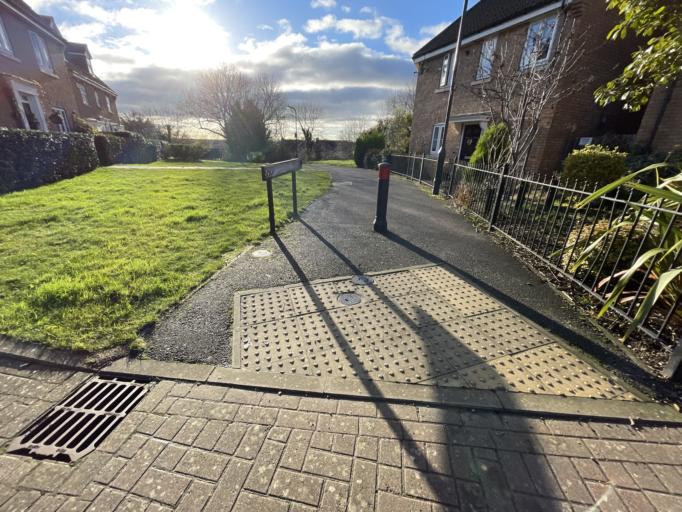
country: GB
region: England
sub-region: Warwickshire
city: Rugby
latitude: 52.3972
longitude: -1.2390
